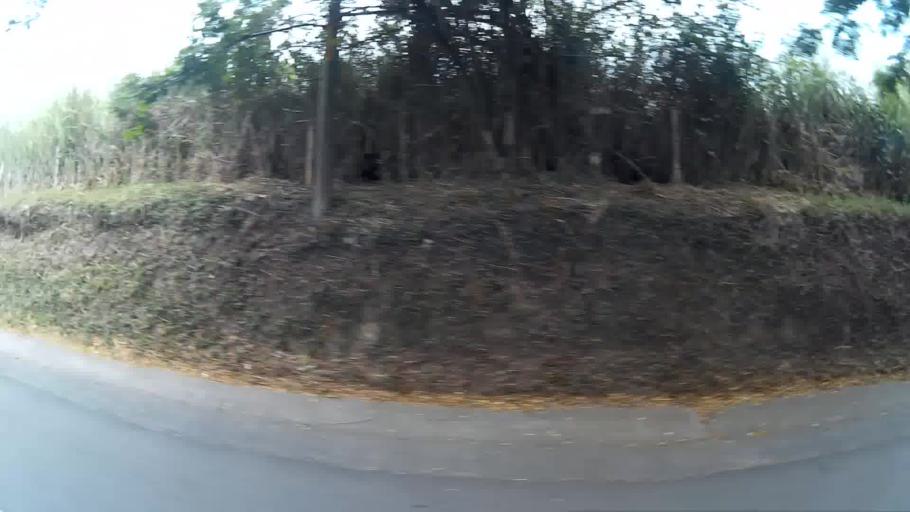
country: CO
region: Risaralda
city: Pereira
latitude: 4.8130
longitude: -75.8064
